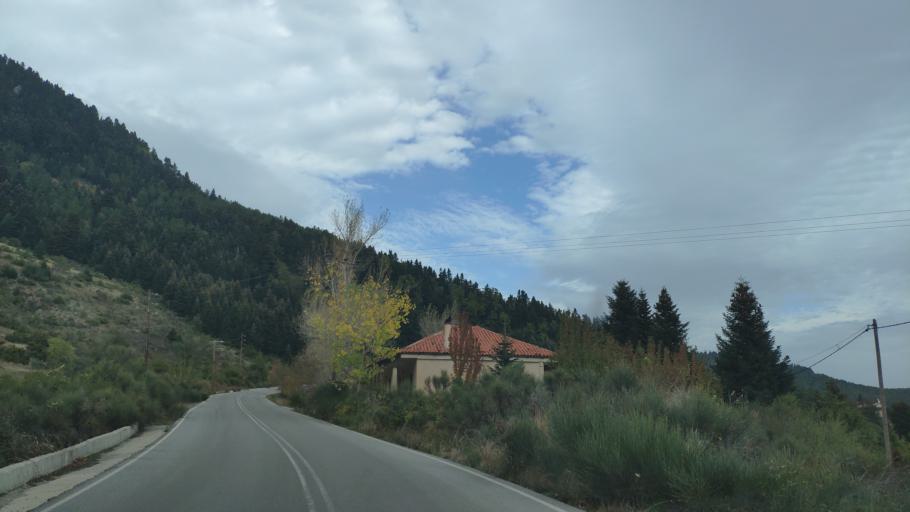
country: GR
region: Central Greece
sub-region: Nomos Fokidos
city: Amfissa
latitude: 38.6858
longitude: 22.3197
